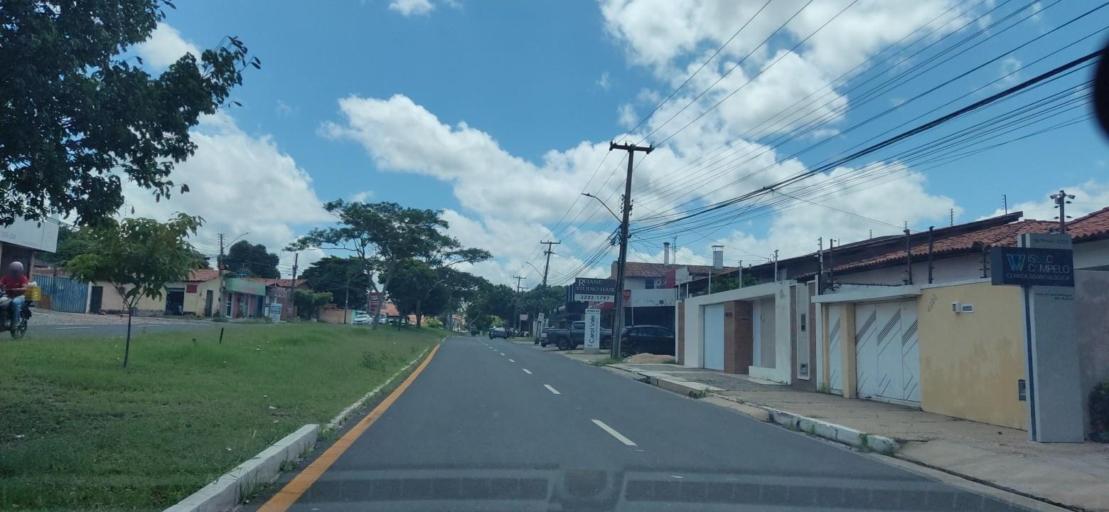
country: BR
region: Piaui
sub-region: Teresina
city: Teresina
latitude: -5.0649
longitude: -42.7654
